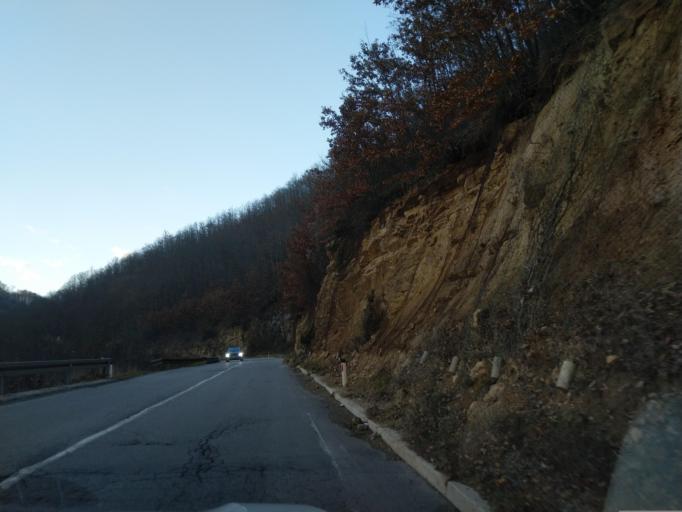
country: RS
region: Central Serbia
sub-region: Zlatiborski Okrug
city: Kosjeric
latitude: 43.9670
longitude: 19.9589
